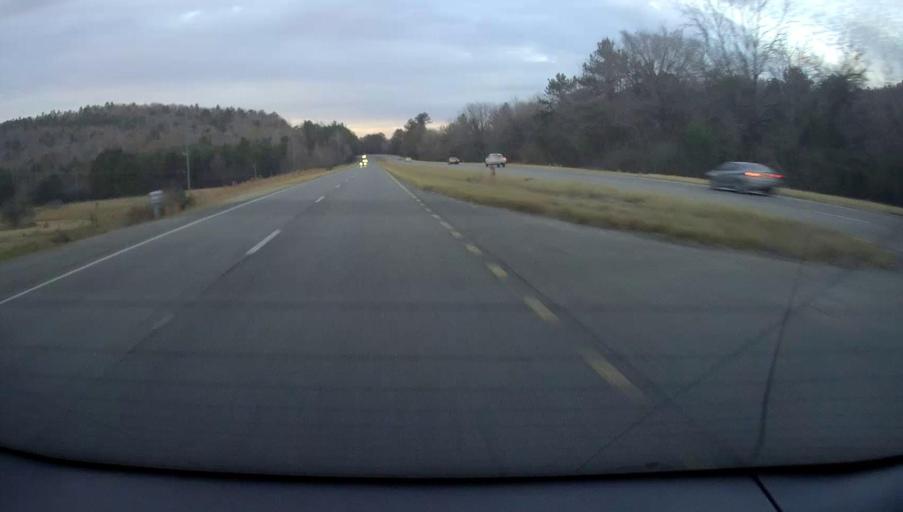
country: US
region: Alabama
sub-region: Etowah County
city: Glencoe
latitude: 33.9296
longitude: -85.9132
